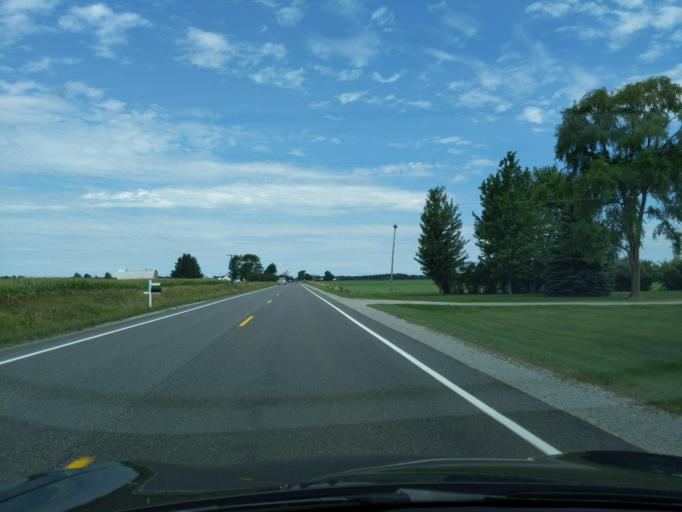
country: US
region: Michigan
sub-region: Gratiot County
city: Breckenridge
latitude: 43.4900
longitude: -84.3698
